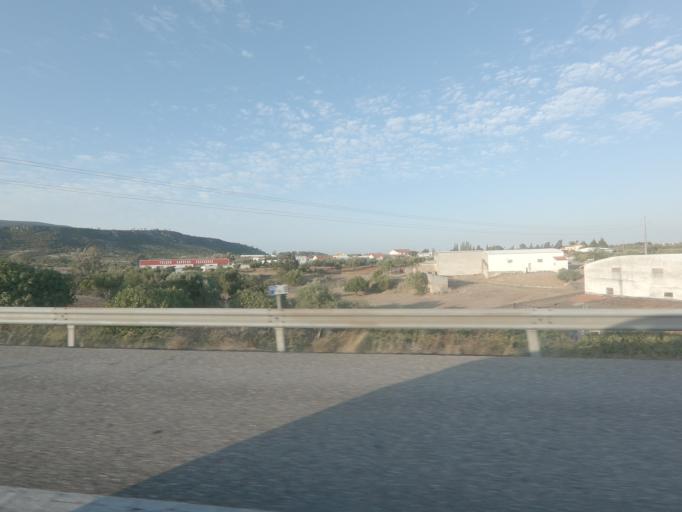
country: PT
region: Santarem
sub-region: Alcanena
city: Alcanena
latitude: 39.4817
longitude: -8.6354
